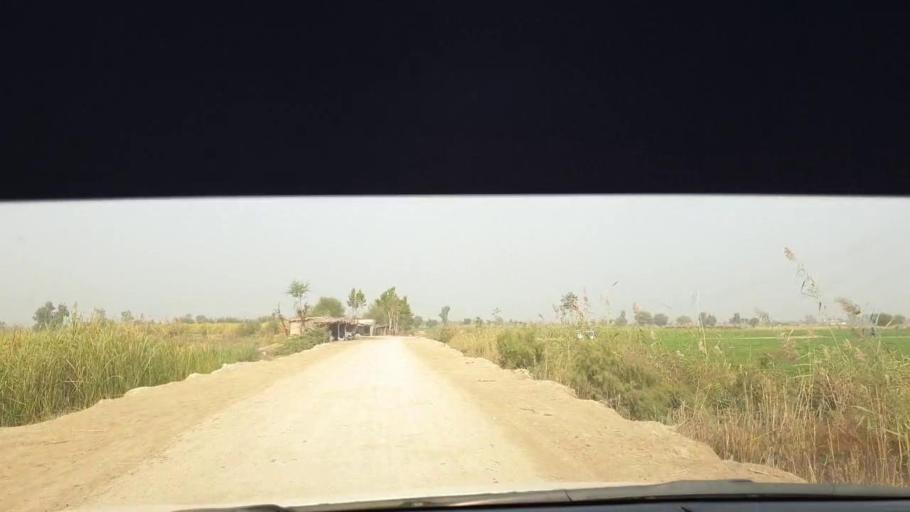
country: PK
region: Sindh
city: Berani
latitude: 25.8184
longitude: 68.8434
